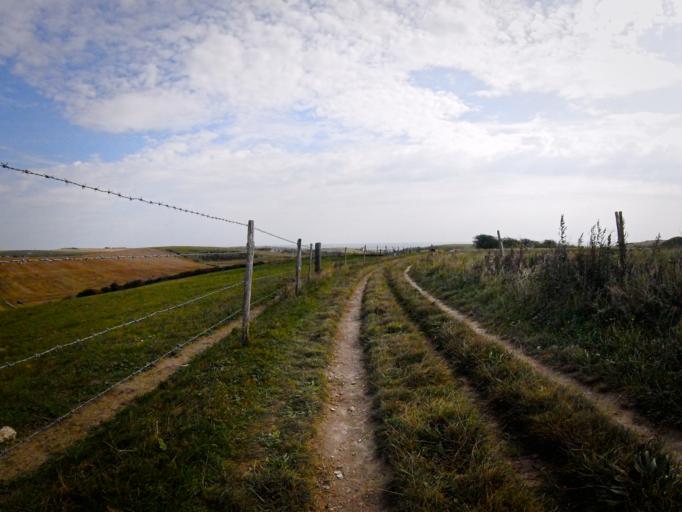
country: GB
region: England
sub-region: Brighton and Hove
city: Rottingdean
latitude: 50.8288
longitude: -0.0875
